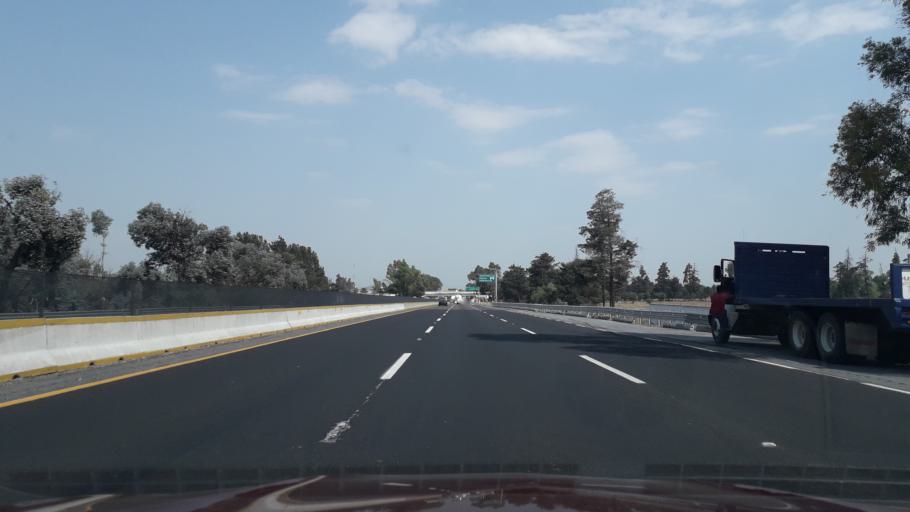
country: MX
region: Puebla
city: San Martin Texmelucan de Labastida
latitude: 19.2744
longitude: -98.4370
